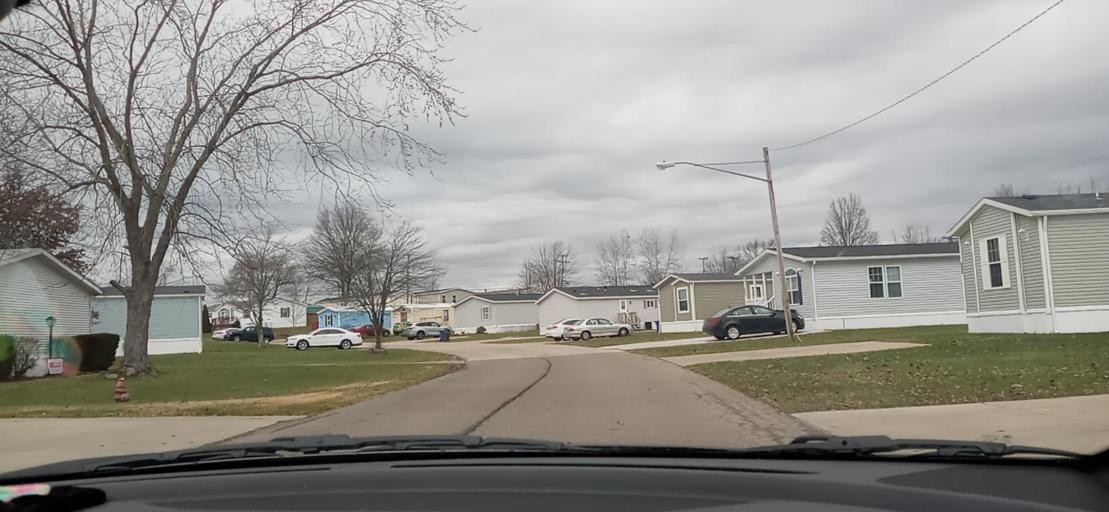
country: US
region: Ohio
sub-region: Portage County
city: Ravenna
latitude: 41.1201
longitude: -81.2329
